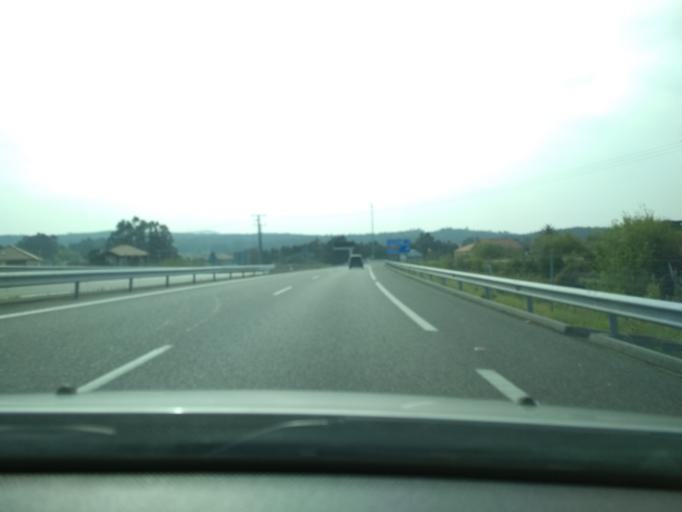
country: ES
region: Galicia
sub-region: Provincia da Coruna
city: Rianxo
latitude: 42.6684
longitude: -8.8172
